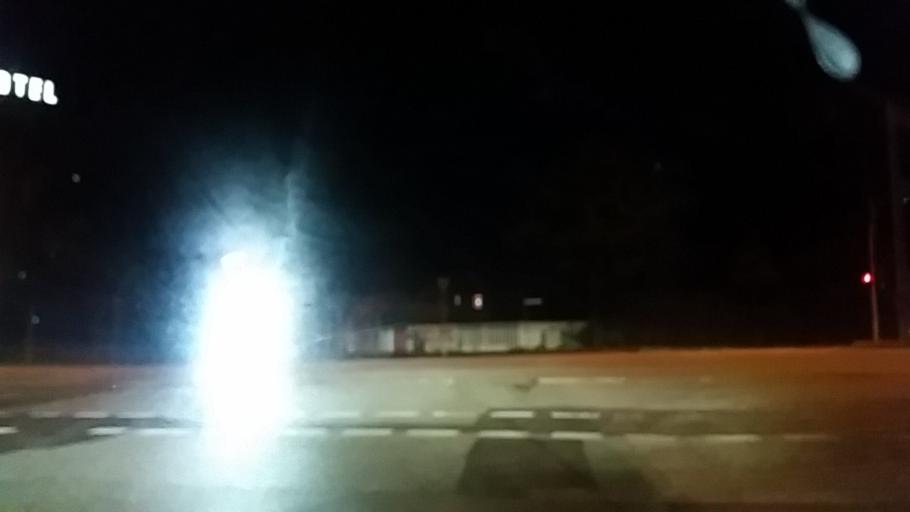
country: DE
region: Hamburg
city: Marienthal
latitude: 53.5390
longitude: 10.0841
